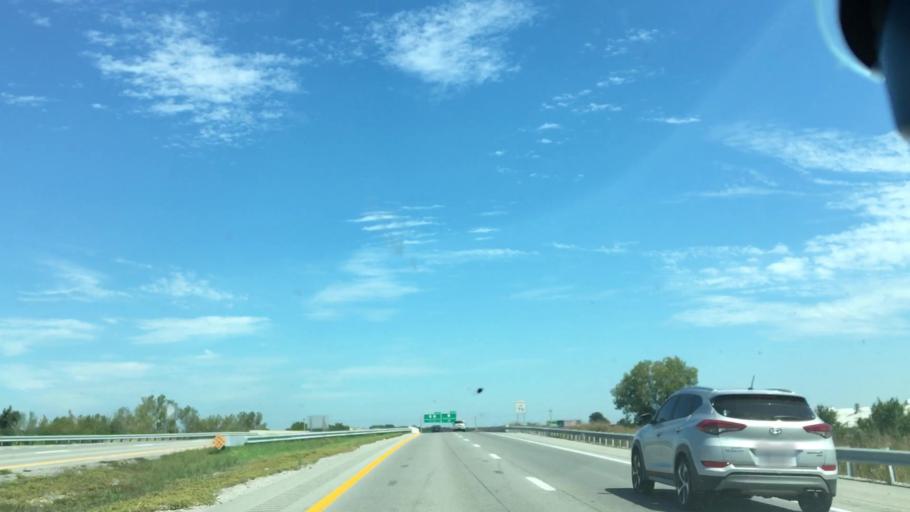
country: US
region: Kentucky
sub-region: Christian County
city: Hopkinsville
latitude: 36.8388
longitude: -87.4681
